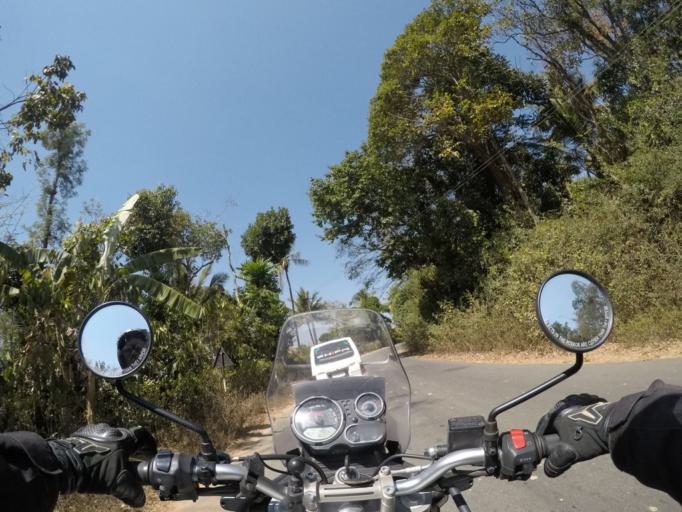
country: IN
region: Karnataka
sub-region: Chikmagalur
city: Mudigere
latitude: 13.0616
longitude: 75.6754
